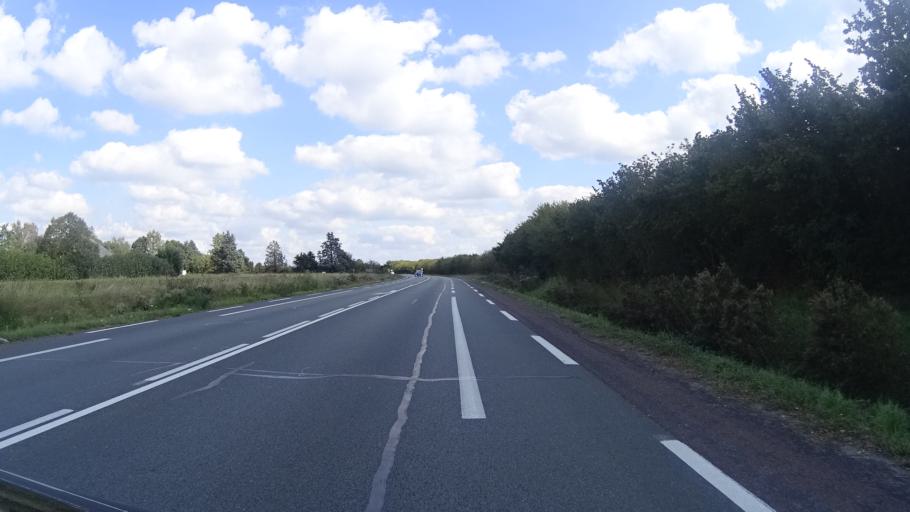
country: FR
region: Pays de la Loire
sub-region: Departement de Maine-et-Loire
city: Sainte-Gemmes-sur-Loire
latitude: 47.4208
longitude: -0.5795
